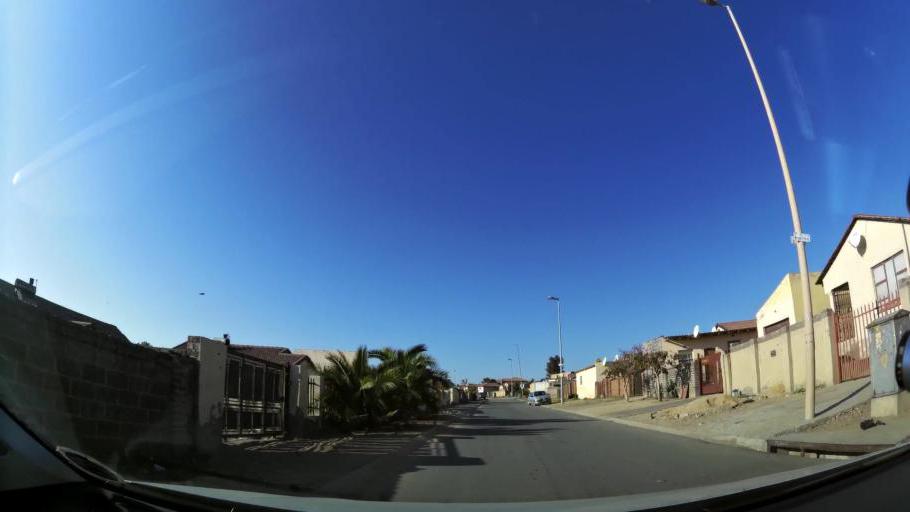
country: ZA
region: Gauteng
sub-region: City of Johannesburg Metropolitan Municipality
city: Modderfontein
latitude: -26.0458
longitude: 28.1543
